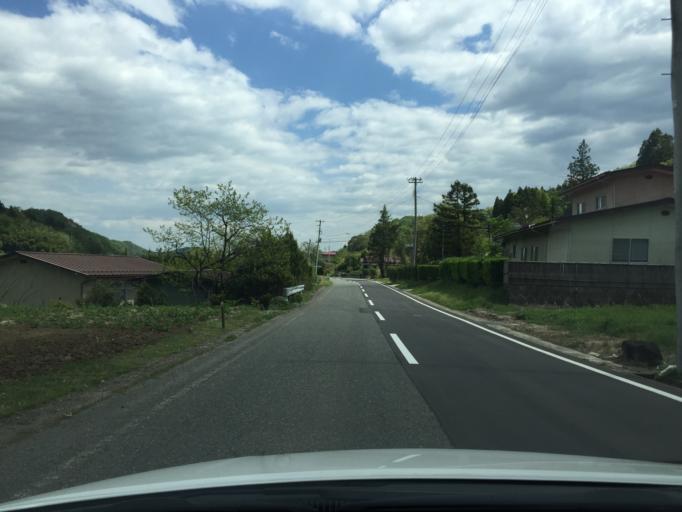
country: JP
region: Fukushima
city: Hobaramachi
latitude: 37.7399
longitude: 140.5601
